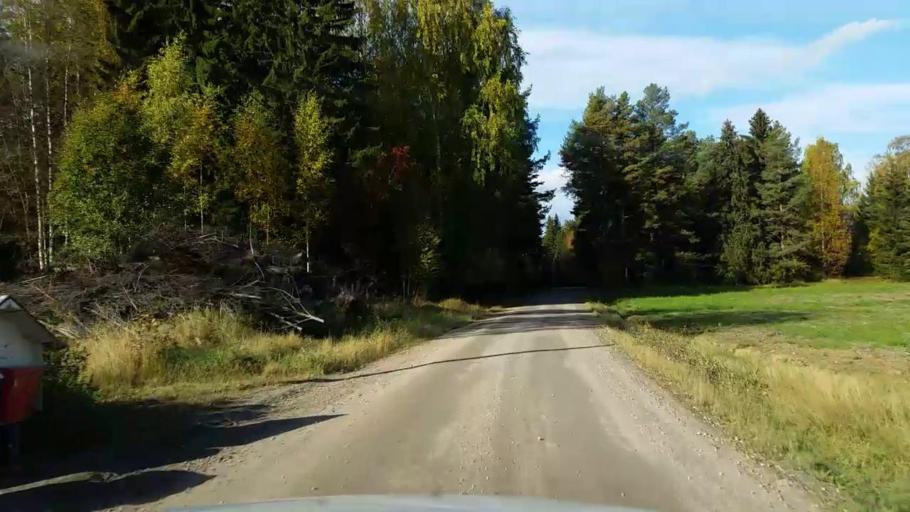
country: SE
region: Gaevleborg
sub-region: Ljusdals Kommun
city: Jaervsoe
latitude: 61.7895
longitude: 16.1867
